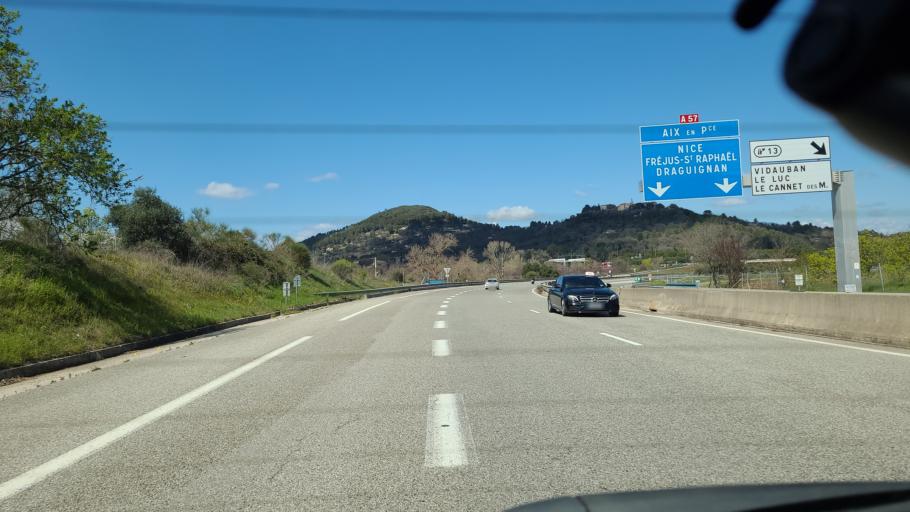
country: FR
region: Provence-Alpes-Cote d'Azur
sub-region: Departement du Var
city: Le Cannet-des-Maures
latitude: 43.3892
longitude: 6.3553
